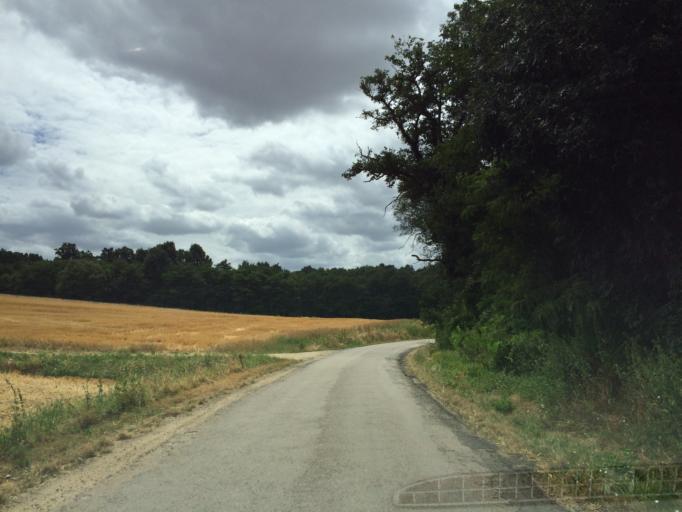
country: FR
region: Bourgogne
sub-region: Departement de l'Yonne
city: Fleury-la-Vallee
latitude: 47.8431
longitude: 3.4102
